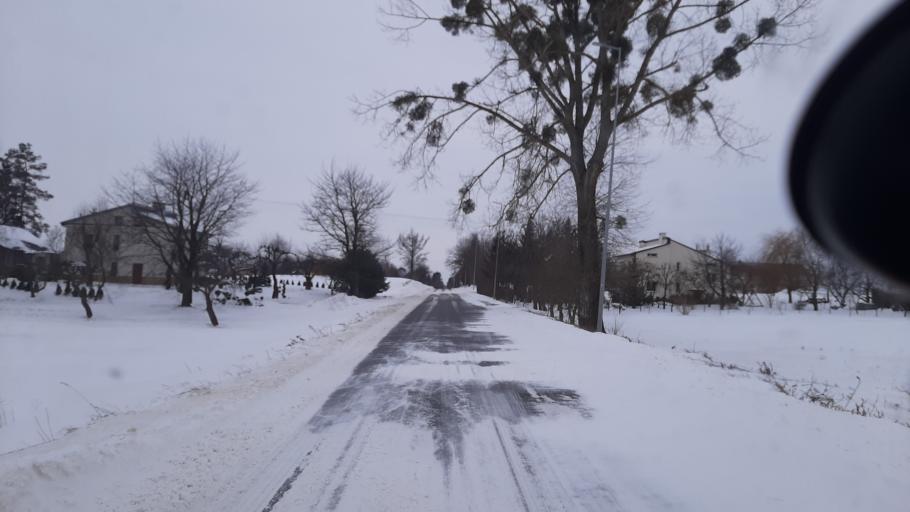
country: PL
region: Lublin Voivodeship
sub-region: Powiat lubelski
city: Garbow
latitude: 51.3241
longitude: 22.3239
